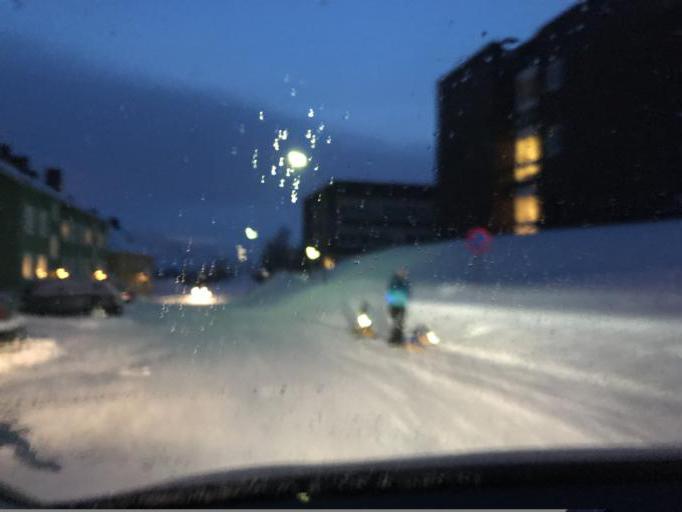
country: SE
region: Norrbotten
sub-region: Kiruna Kommun
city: Kiruna
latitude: 67.8485
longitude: 20.2323
